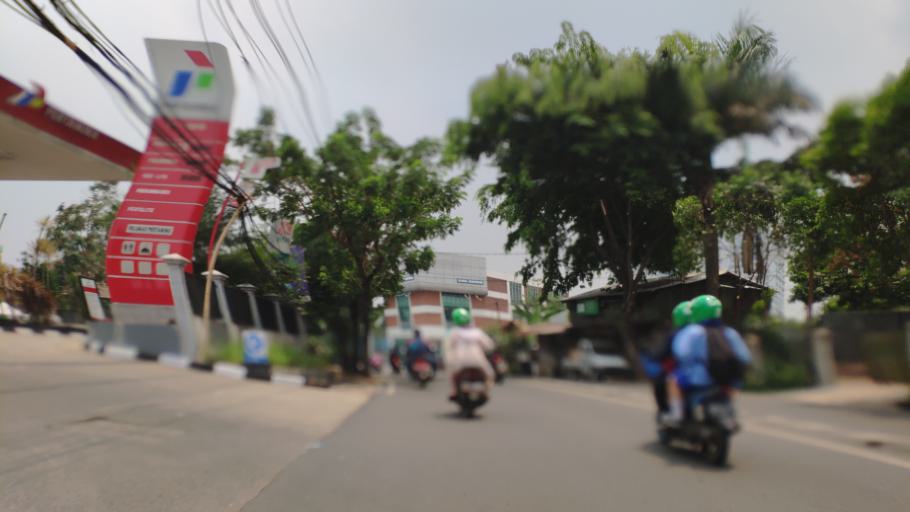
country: ID
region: Banten
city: South Tangerang
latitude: -6.2603
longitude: 106.7768
